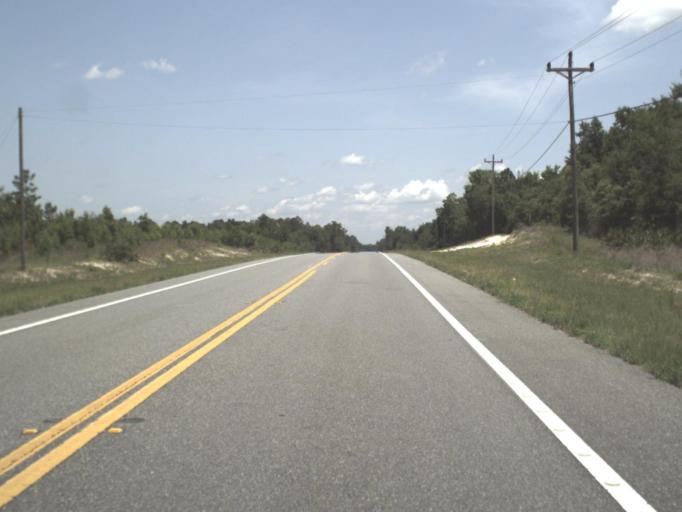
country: US
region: Florida
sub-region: Taylor County
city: Steinhatchee
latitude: 29.7126
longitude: -83.3586
